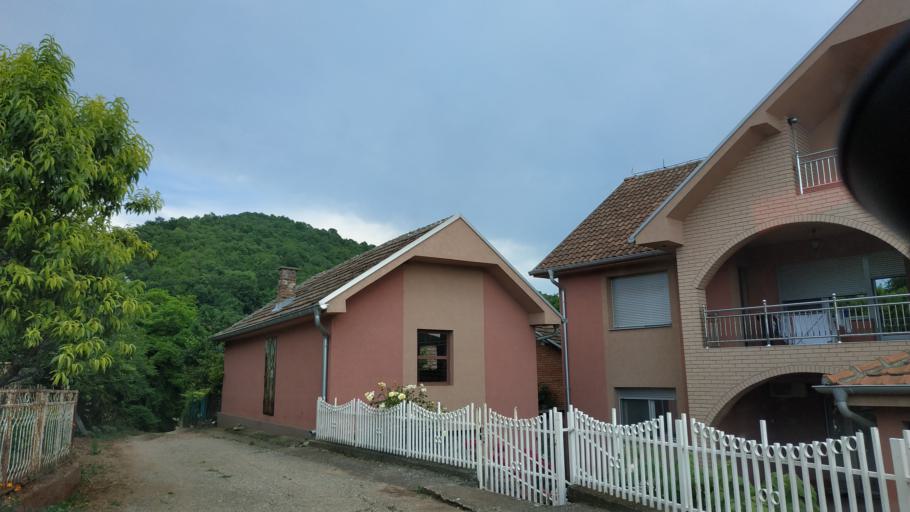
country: RS
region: Central Serbia
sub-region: Nisavski Okrug
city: Aleksinac
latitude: 43.6032
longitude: 21.6957
